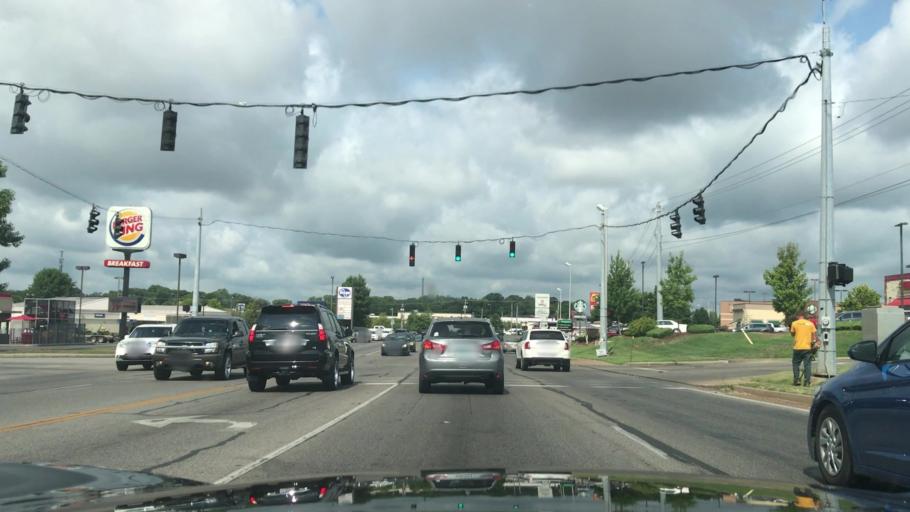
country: US
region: Kentucky
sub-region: Warren County
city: Bowling Green
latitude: 36.9618
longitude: -86.4649
